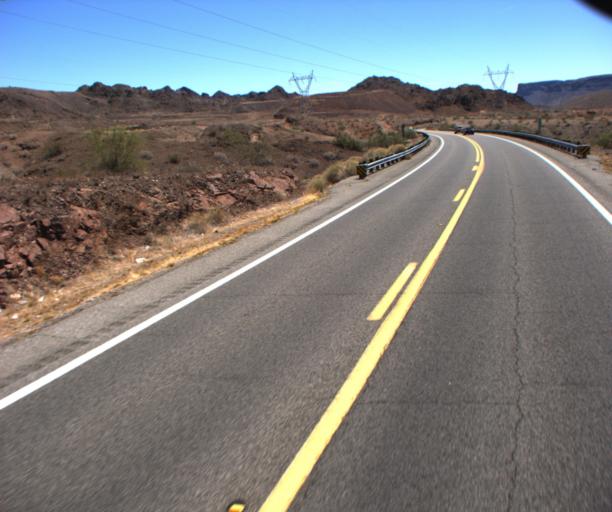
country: US
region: Arizona
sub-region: La Paz County
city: Cienega Springs
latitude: 34.3407
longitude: -114.1447
